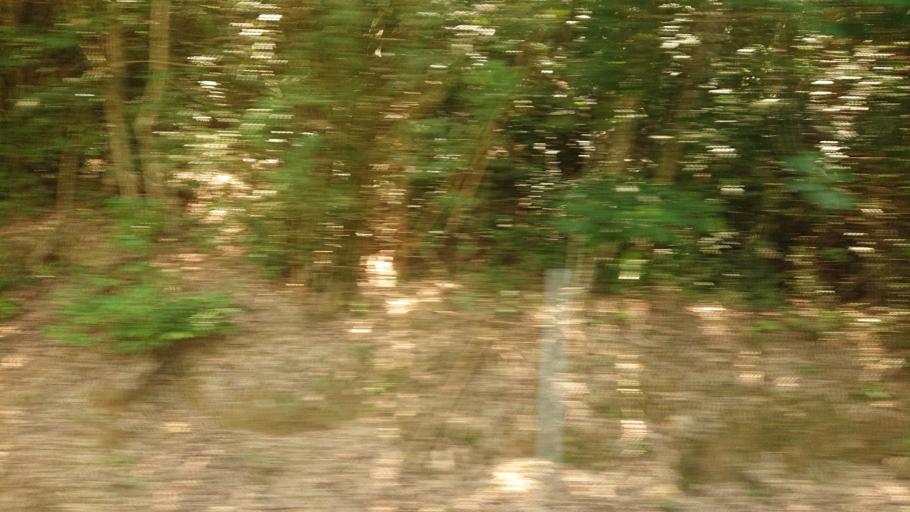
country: TW
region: Taiwan
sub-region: Nantou
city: Puli
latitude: 24.0500
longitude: 120.9358
